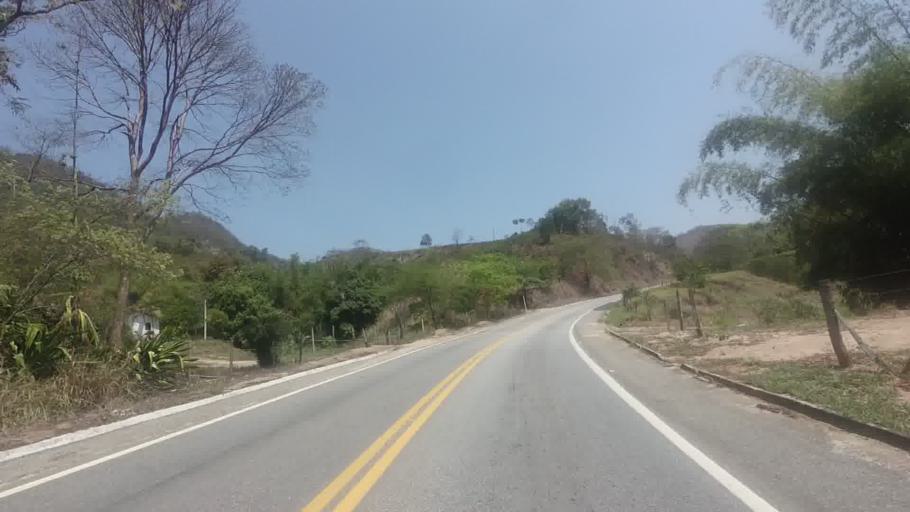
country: BR
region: Espirito Santo
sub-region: Cachoeiro De Itapemirim
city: Cachoeiro de Itapemirim
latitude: -20.8393
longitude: -41.2317
